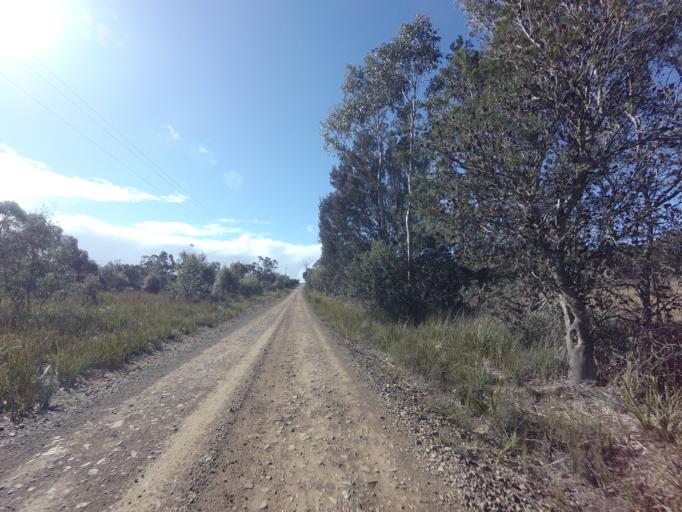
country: AU
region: Tasmania
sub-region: Sorell
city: Sorell
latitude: -42.3502
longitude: 147.9719
